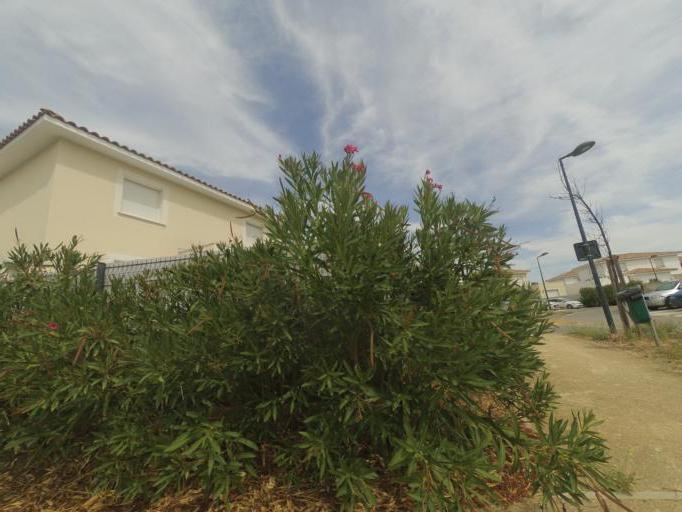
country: FR
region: Languedoc-Roussillon
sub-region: Departement du Gard
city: Aimargues
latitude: 43.7018
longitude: 4.2014
